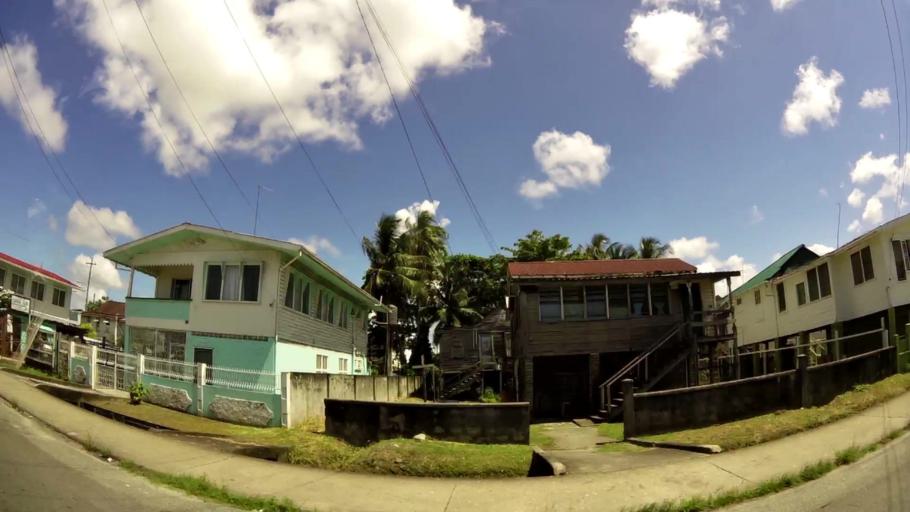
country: GY
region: Demerara-Mahaica
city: Georgetown
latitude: 6.8043
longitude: -58.1580
